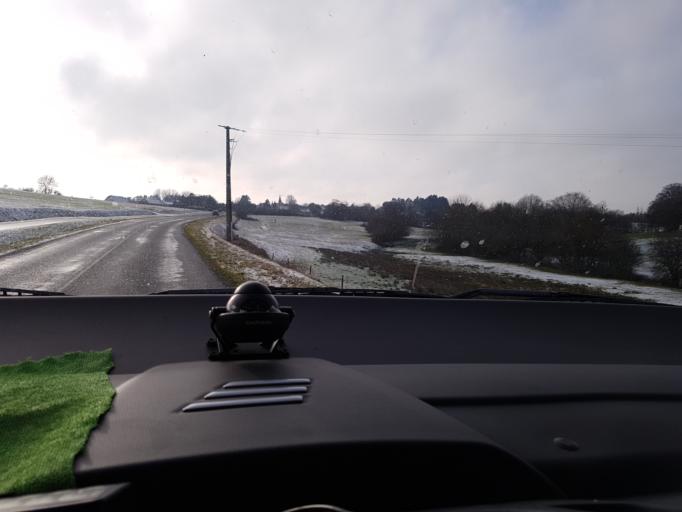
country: FR
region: Champagne-Ardenne
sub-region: Departement des Ardennes
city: Signy-le-Petit
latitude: 49.8662
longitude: 4.3678
